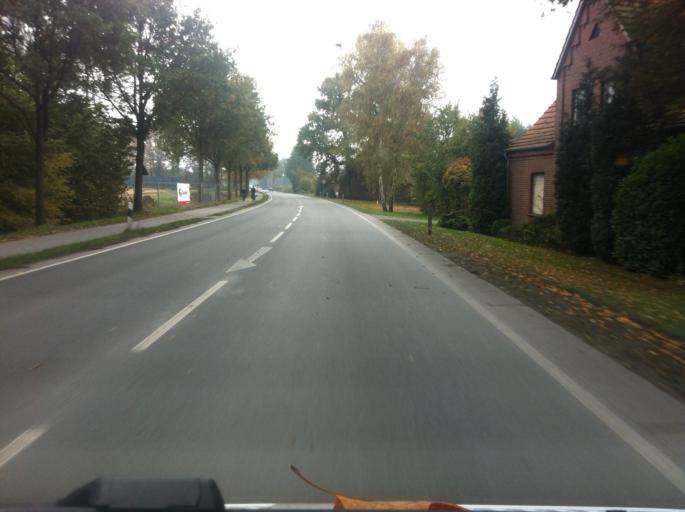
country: DE
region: North Rhine-Westphalia
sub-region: Regierungsbezirk Munster
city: Vreden
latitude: 52.0176
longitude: 6.8219
